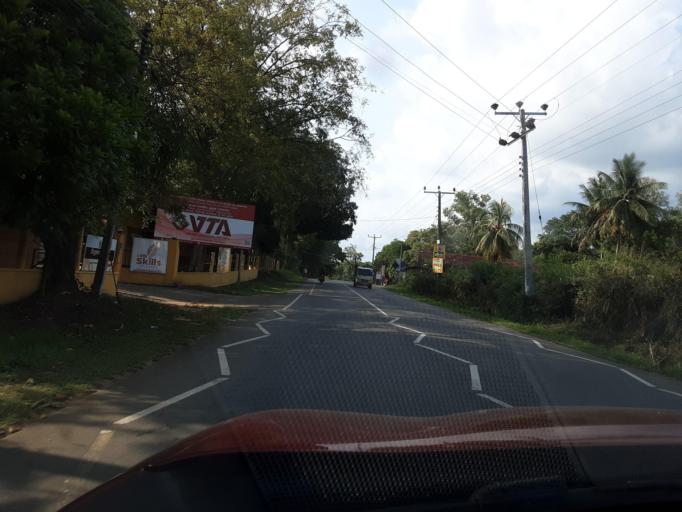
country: LK
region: Uva
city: Haputale
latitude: 6.6737
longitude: 81.1122
